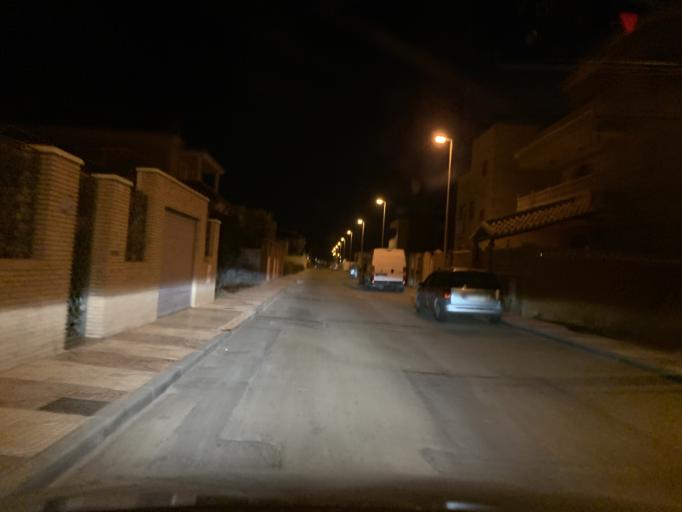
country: ES
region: Andalusia
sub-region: Provincia de Almeria
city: Roquetas de Mar
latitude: 36.7755
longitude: -2.6024
